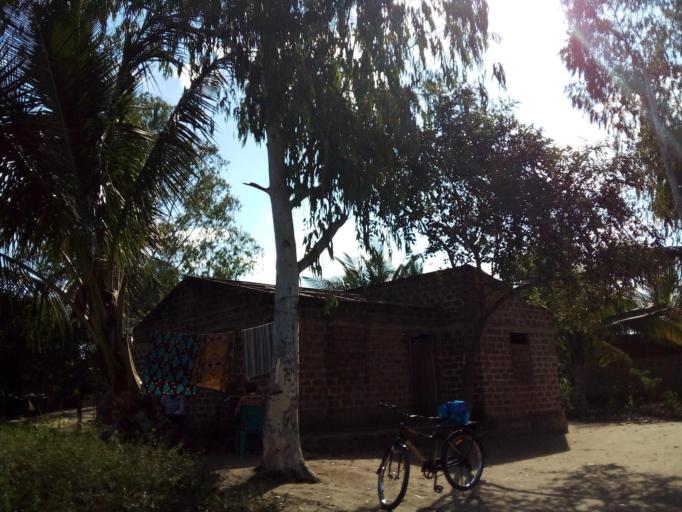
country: MZ
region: Zambezia
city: Quelimane
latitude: -17.5776
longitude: 36.7042
